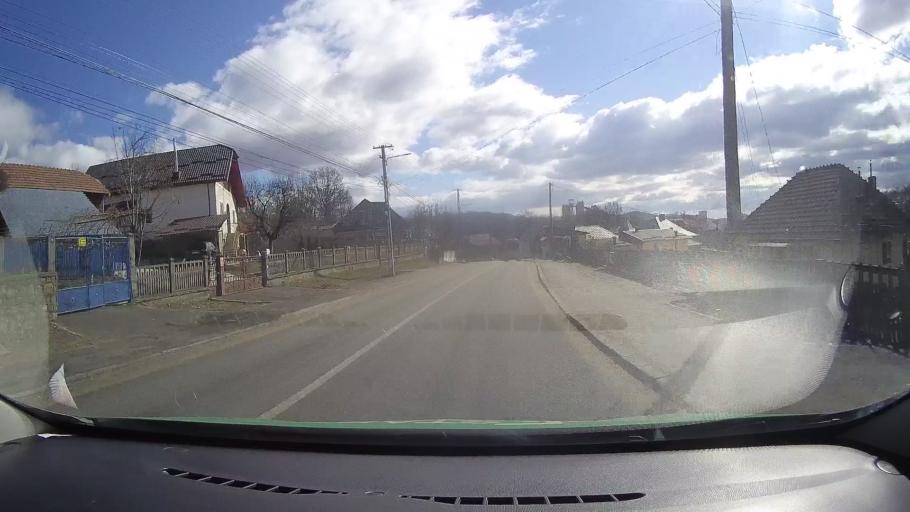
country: RO
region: Dambovita
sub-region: Comuna Fieni
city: Fieni
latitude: 45.1295
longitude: 25.4105
